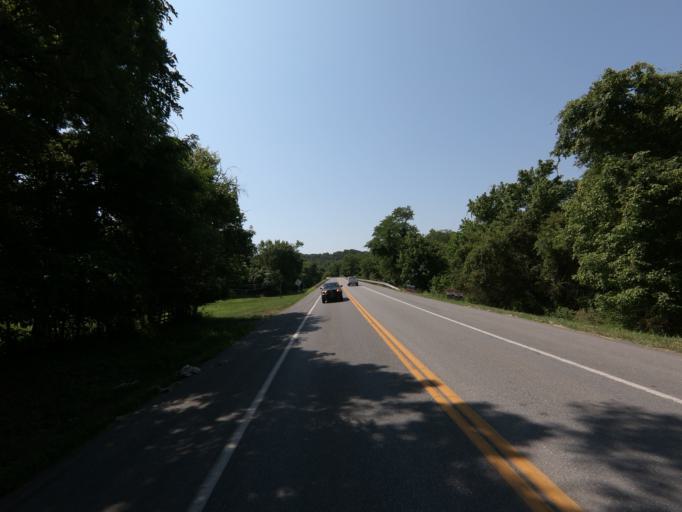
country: US
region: Maryland
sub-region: Frederick County
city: Bartonsville
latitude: 39.3902
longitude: -77.3820
